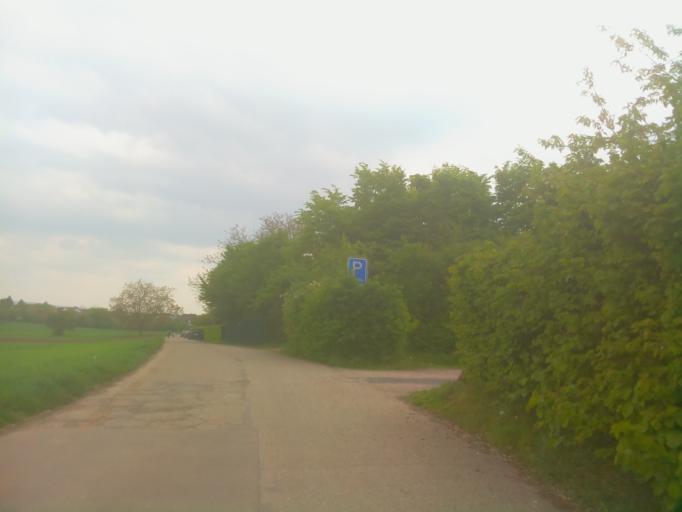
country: DE
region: Baden-Wuerttemberg
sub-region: Karlsruhe Region
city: Plankstadt
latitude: 49.4009
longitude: 8.5896
